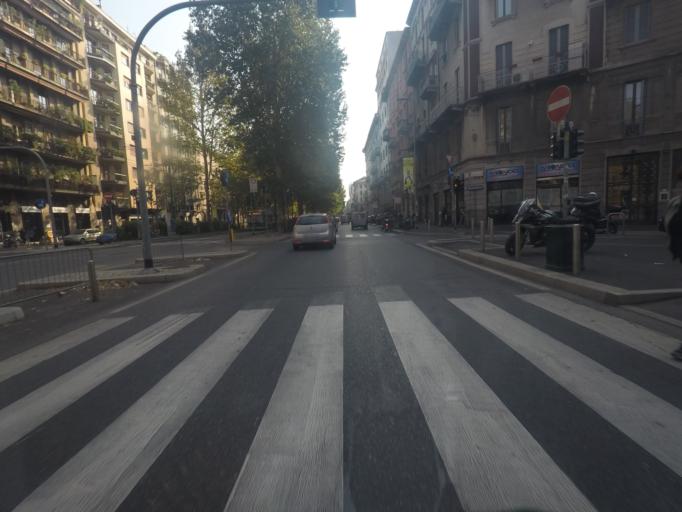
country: IT
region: Lombardy
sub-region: Citta metropolitana di Milano
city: Milano
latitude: 45.4804
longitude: 9.2170
